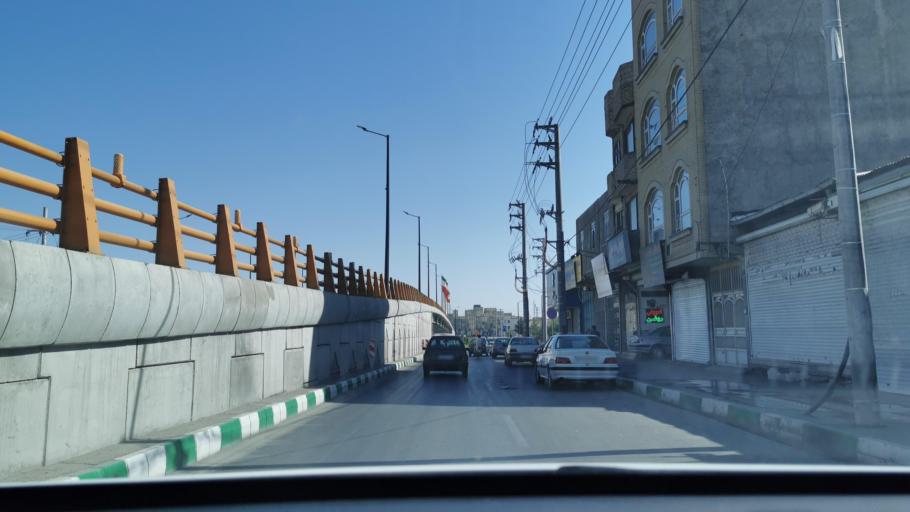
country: IR
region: Razavi Khorasan
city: Mashhad
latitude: 36.3352
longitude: 59.6043
